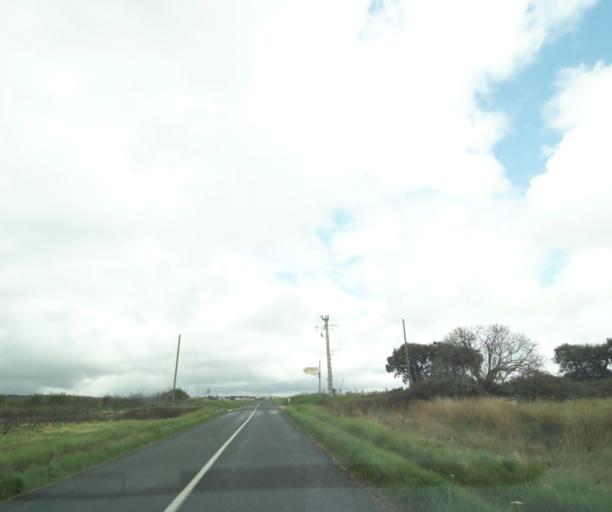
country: FR
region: Languedoc-Roussillon
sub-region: Departement de l'Herault
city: Cournonsec
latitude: 43.5357
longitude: 3.6978
